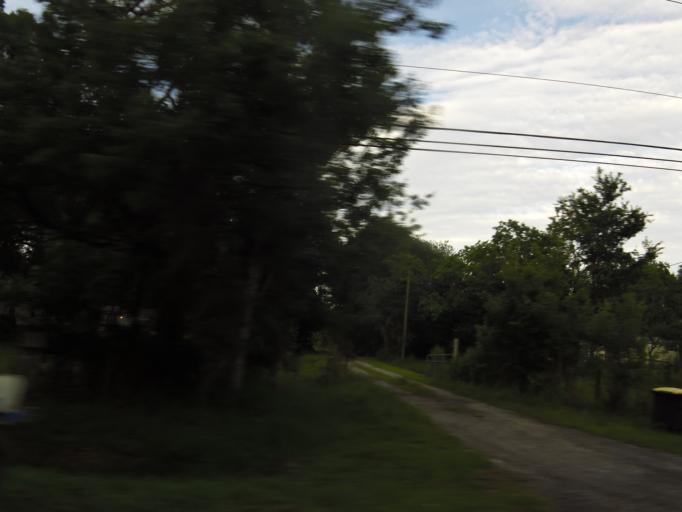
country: US
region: Florida
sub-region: Duval County
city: Jacksonville
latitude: 30.3383
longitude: -81.8067
